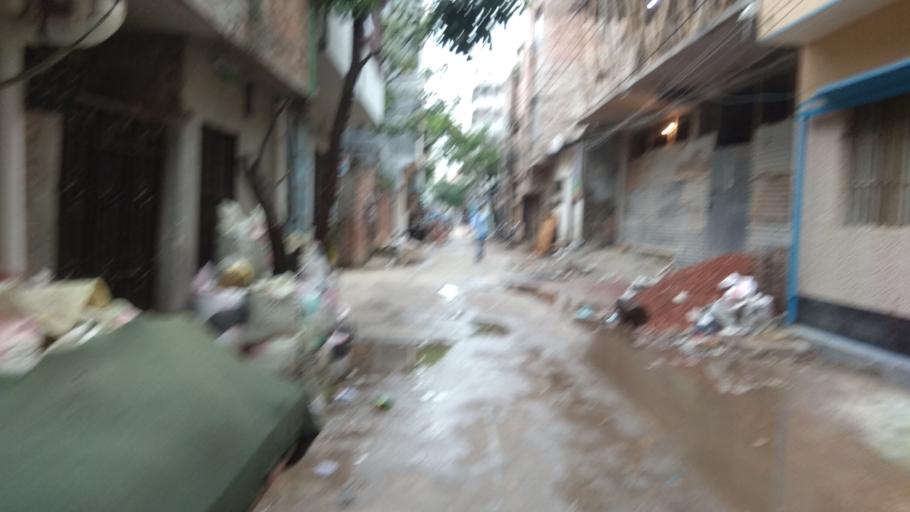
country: BD
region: Dhaka
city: Tungi
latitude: 23.8239
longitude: 90.3705
